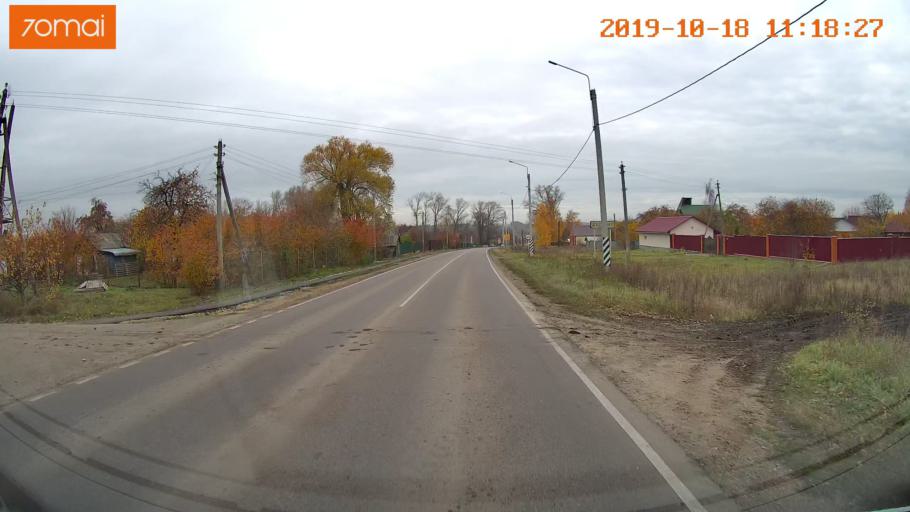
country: RU
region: Tula
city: Kimovsk
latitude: 54.0392
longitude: 38.5503
